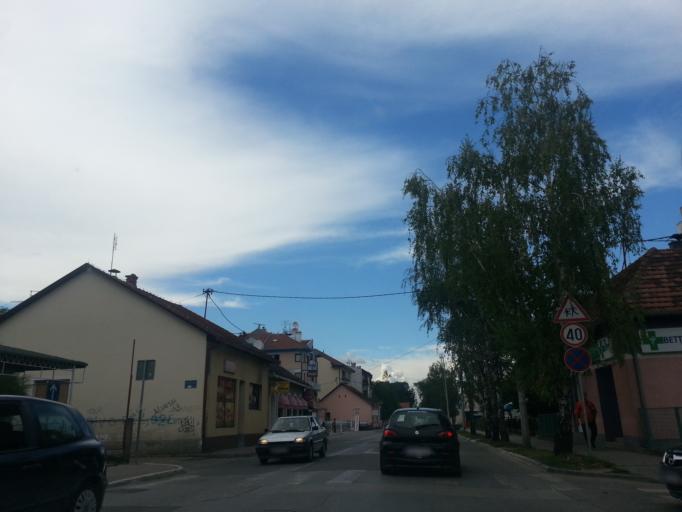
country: BA
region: Brcko
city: Brcko
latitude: 44.8674
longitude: 18.8107
